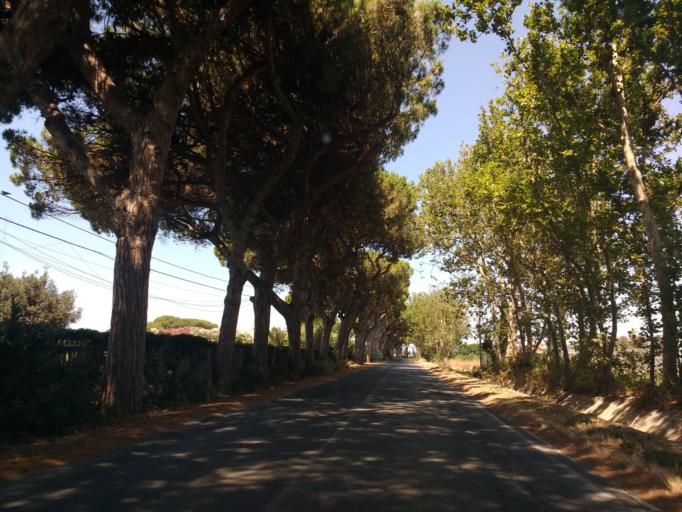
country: IT
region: Latium
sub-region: Citta metropolitana di Roma Capitale
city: Maccarese
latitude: 41.8802
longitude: 12.1989
